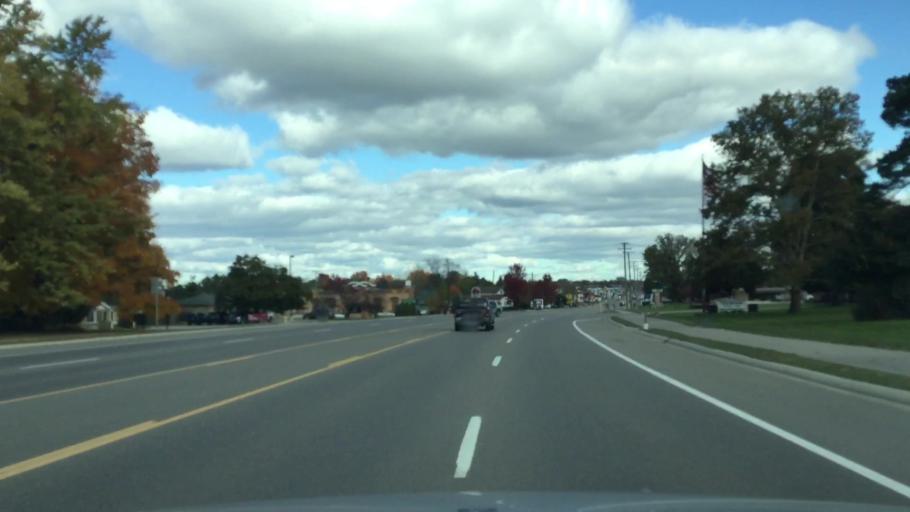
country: US
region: Michigan
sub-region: Lapeer County
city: Lapeer
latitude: 43.0346
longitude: -83.3230
